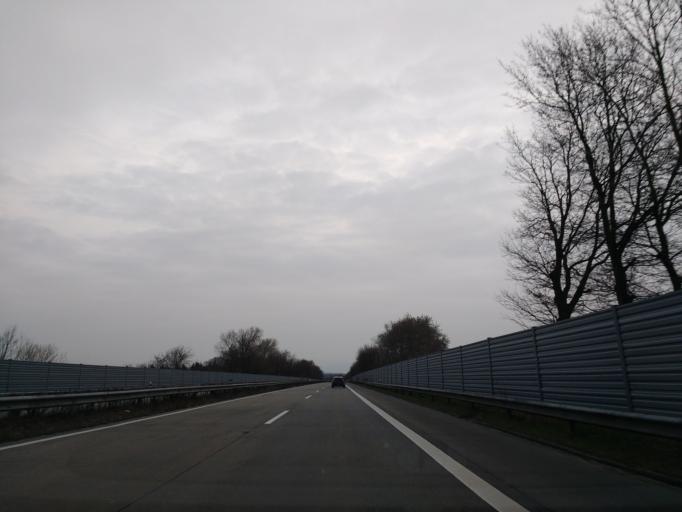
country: DE
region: Lower Saxony
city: Midlum
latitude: 53.7552
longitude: 8.6805
